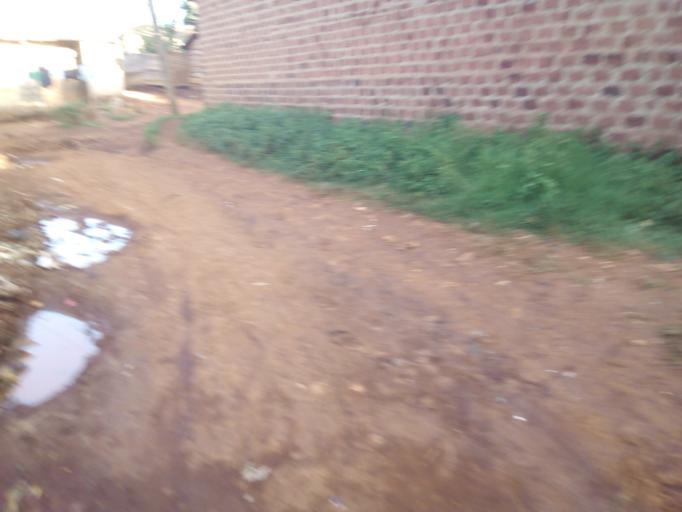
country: UG
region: Central Region
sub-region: Kampala District
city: Kampala
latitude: 0.2530
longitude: 32.5771
